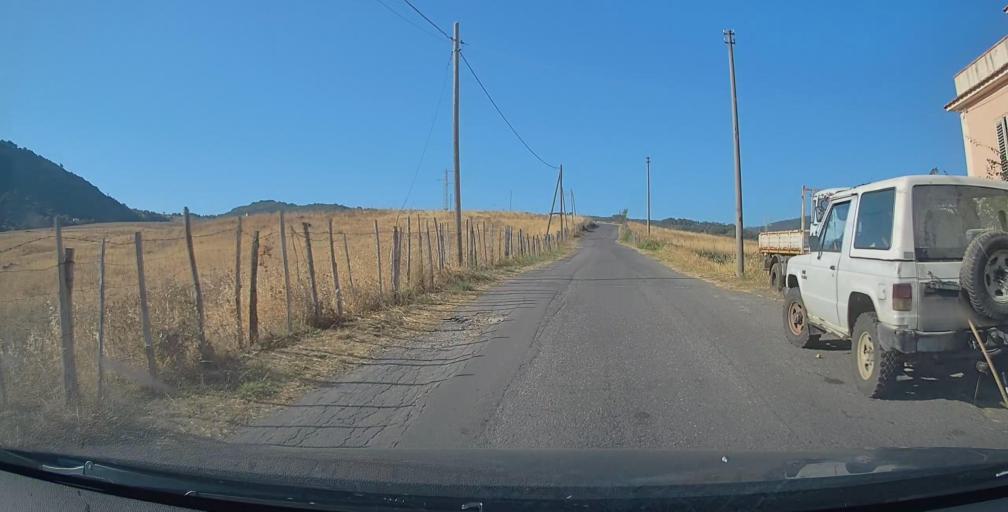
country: IT
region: Sicily
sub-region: Messina
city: San Piero Patti
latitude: 38.0732
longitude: 14.9856
